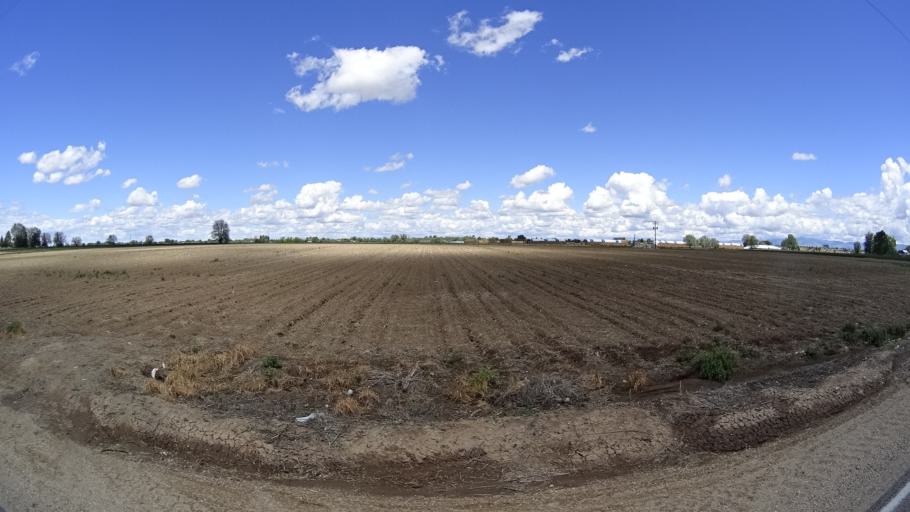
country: US
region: Idaho
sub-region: Ada County
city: Kuna
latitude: 43.5464
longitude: -116.4597
